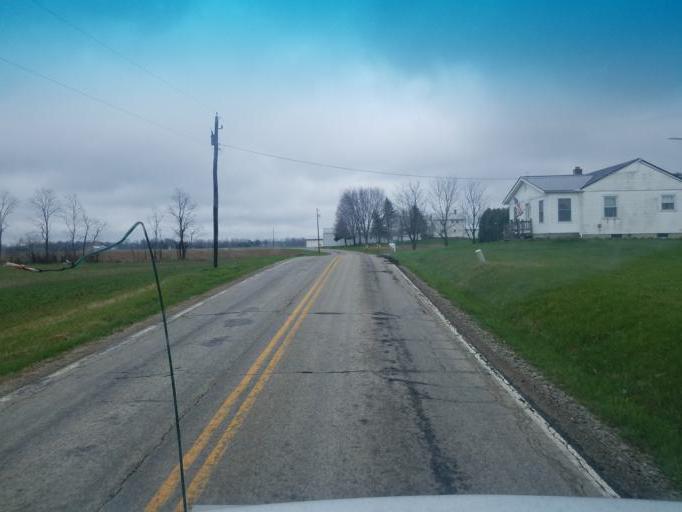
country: US
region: Ohio
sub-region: Richland County
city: Shelby
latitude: 40.9276
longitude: -82.6446
